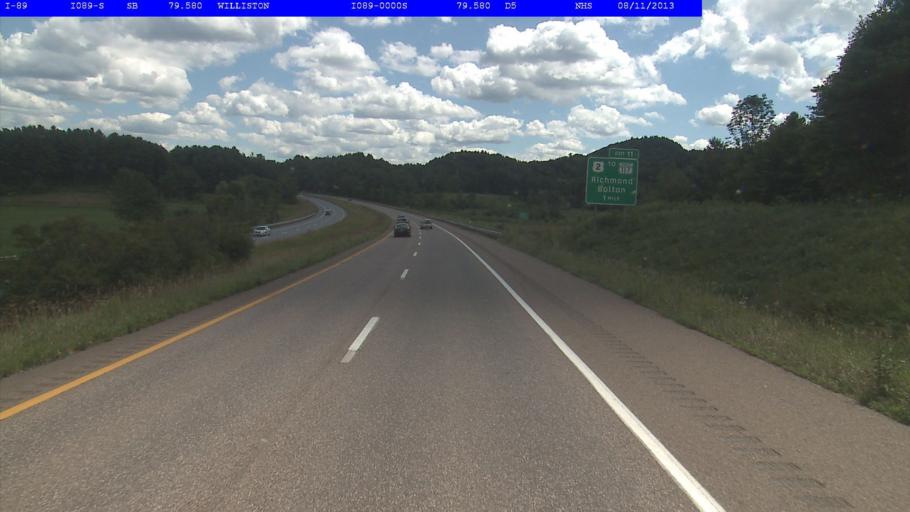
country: US
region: Vermont
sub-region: Chittenden County
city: Williston
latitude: 44.4249
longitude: -73.0326
